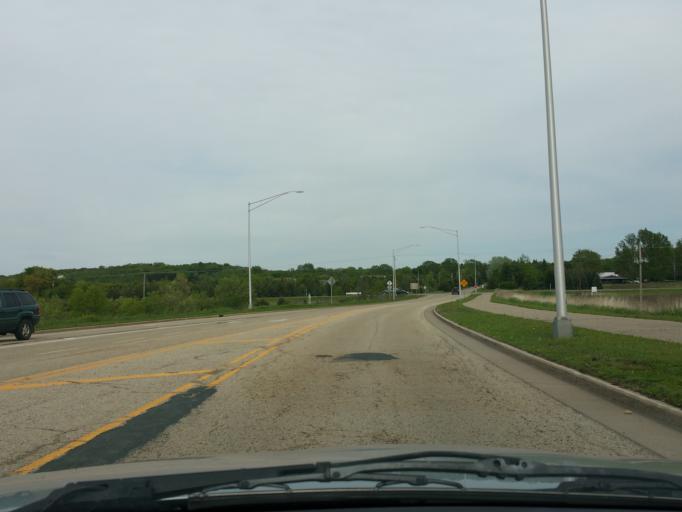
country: US
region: Wisconsin
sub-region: Saint Croix County
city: Hudson
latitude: 44.9487
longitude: -92.6933
